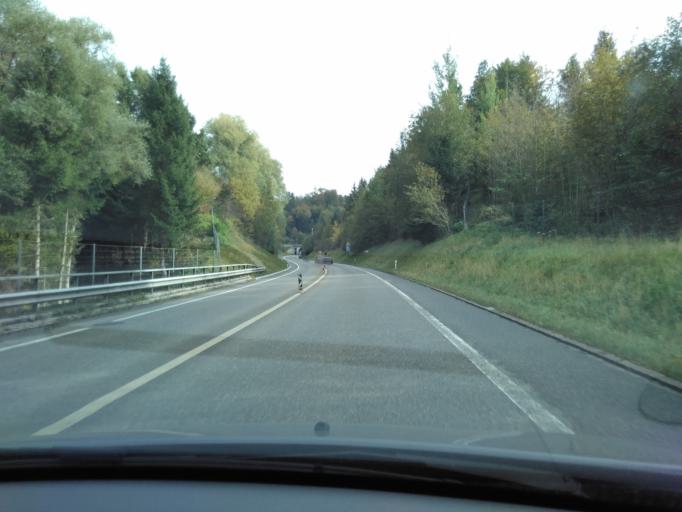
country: CH
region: Zurich
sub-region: Bezirk Hinwil
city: Rueti / Dorfzentrum, Suedl. Teil
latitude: 47.2443
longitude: 8.8546
